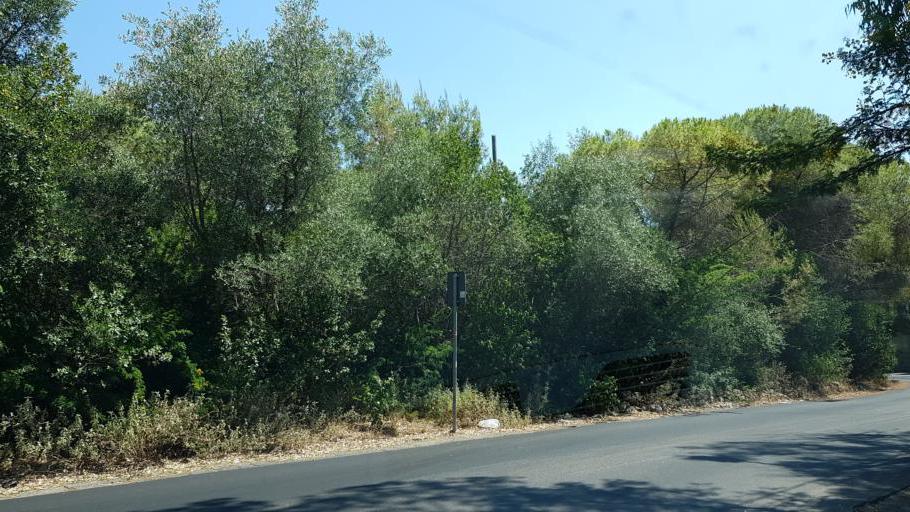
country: IT
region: Apulia
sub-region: Provincia di Lecce
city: Nardo
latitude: 40.1453
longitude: 17.9875
